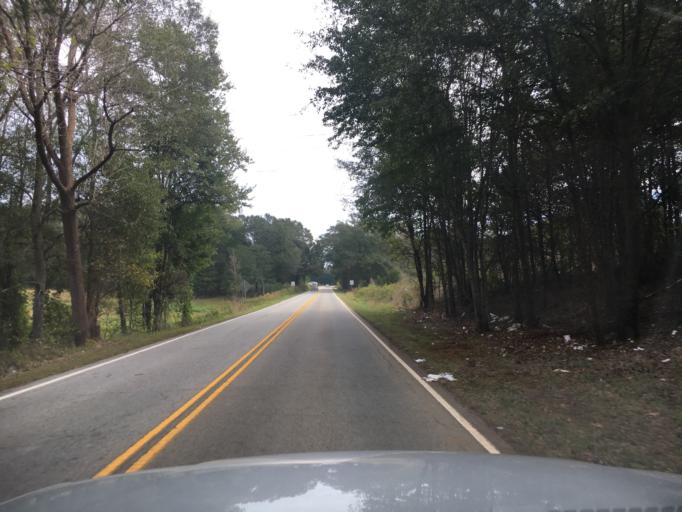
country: US
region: South Carolina
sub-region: Spartanburg County
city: Duncan
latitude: 34.9387
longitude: -82.1580
